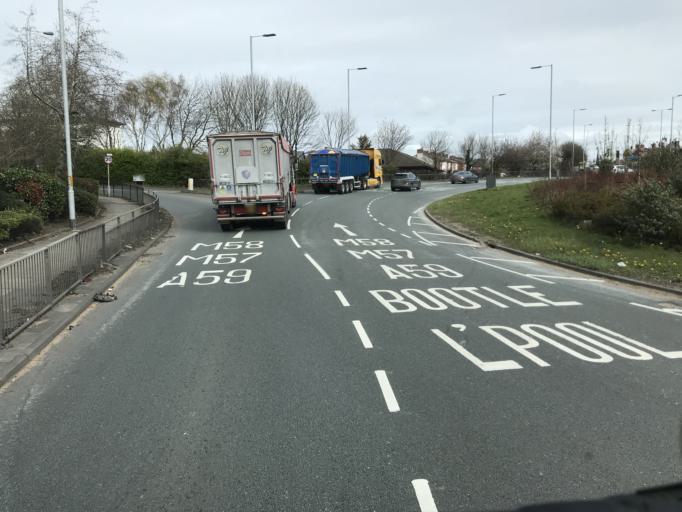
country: GB
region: England
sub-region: Sefton
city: Litherland
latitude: 53.4674
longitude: -3.0052
